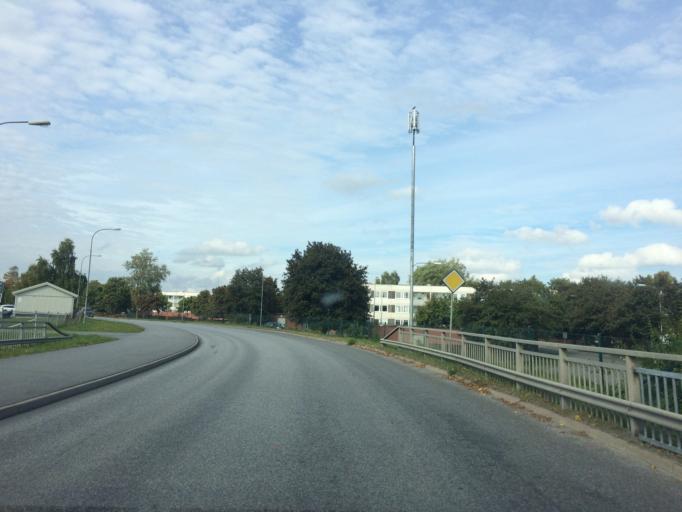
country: SE
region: Stockholm
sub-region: Sollentuna Kommun
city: Sollentuna
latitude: 59.4267
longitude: 17.9406
